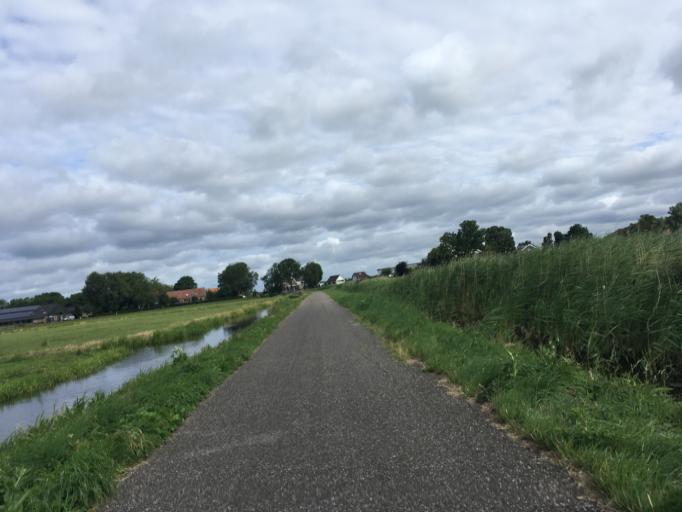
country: NL
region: North Holland
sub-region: Gemeente Haarlem
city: Haarlem
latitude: 52.3941
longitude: 4.6934
